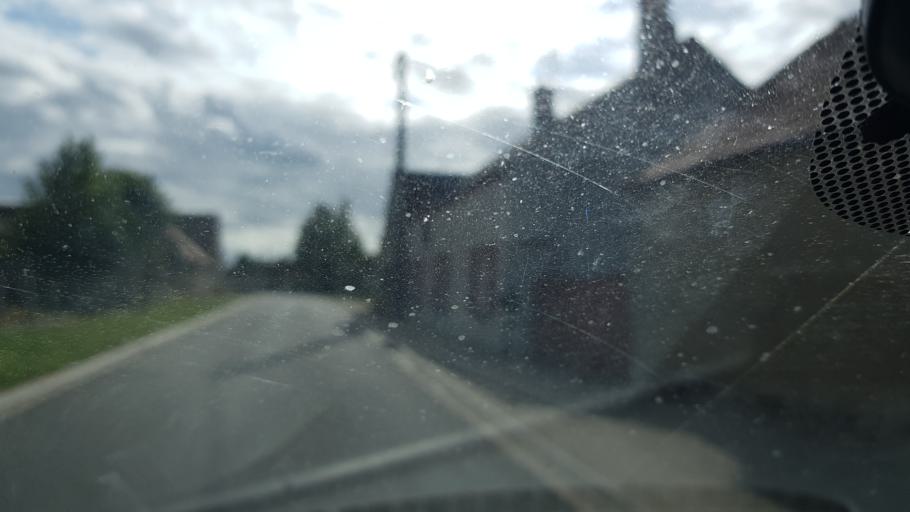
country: FR
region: Centre
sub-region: Departement du Loiret
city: Chilleurs-aux-Bois
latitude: 48.0995
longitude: 2.1926
